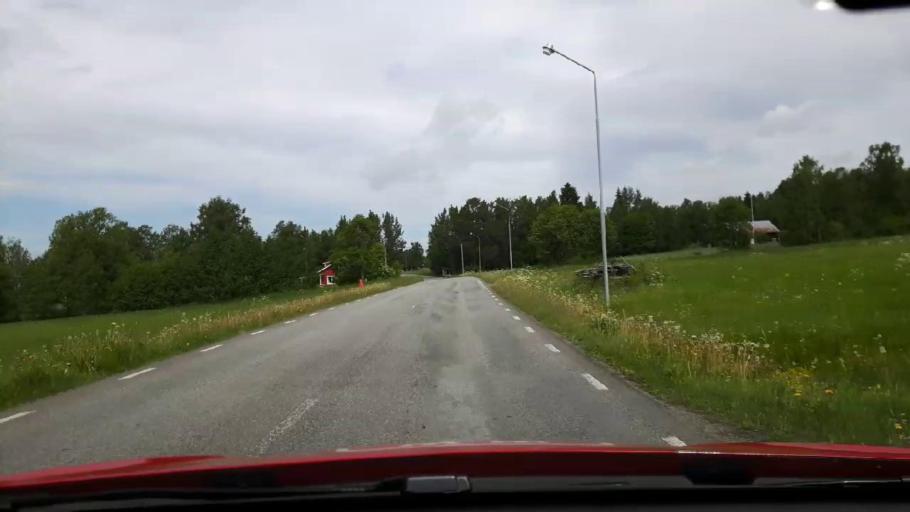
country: SE
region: Jaemtland
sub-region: OEstersunds Kommun
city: Ostersund
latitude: 63.0434
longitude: 14.4565
